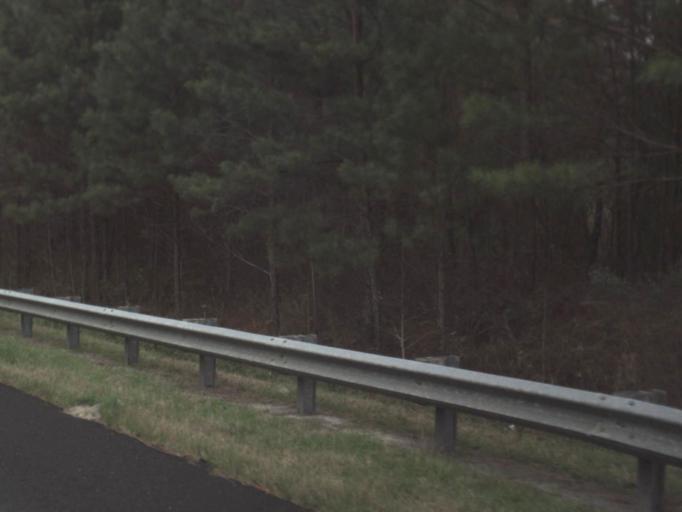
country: US
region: Georgia
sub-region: Grady County
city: Cairo
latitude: 30.6726
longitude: -84.1595
